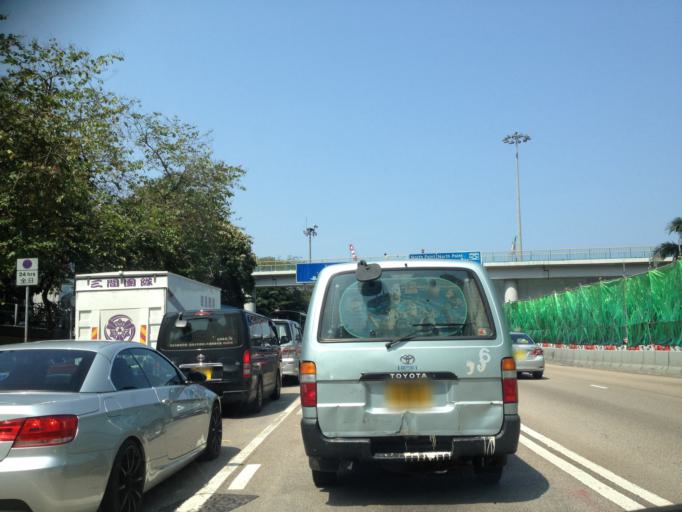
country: HK
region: Wanchai
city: Wan Chai
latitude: 22.2810
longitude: 114.1793
